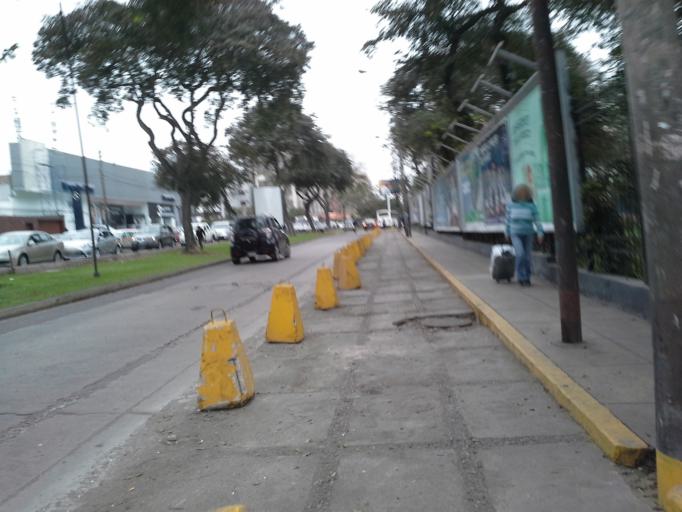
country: PE
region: Lima
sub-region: Lima
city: San Luis
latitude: -12.1023
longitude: -77.0174
